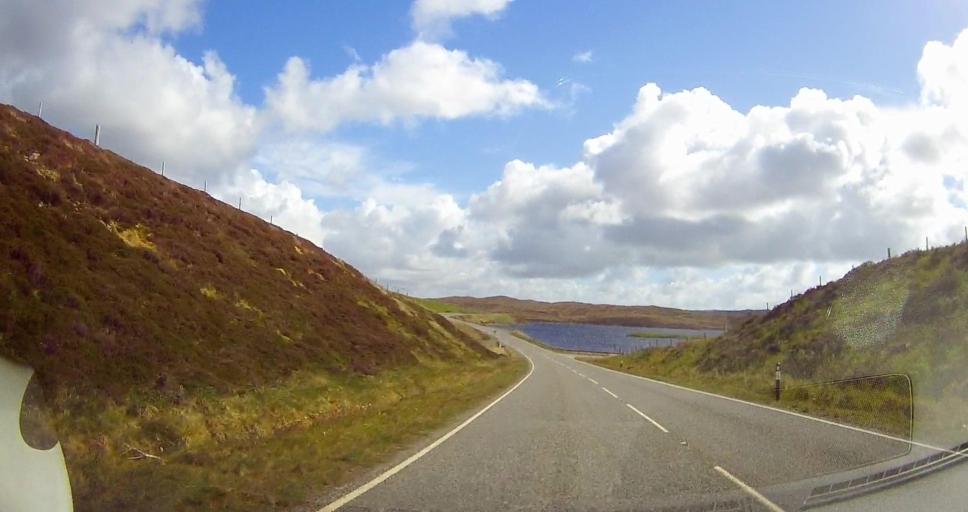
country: GB
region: Scotland
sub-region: Shetland Islands
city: Lerwick
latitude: 60.4686
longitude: -1.4070
